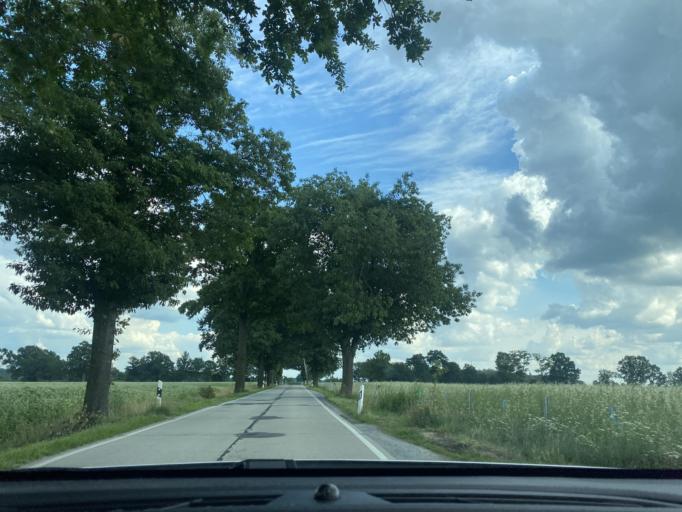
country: DE
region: Saxony
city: Klitten
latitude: 51.3624
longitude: 14.6056
